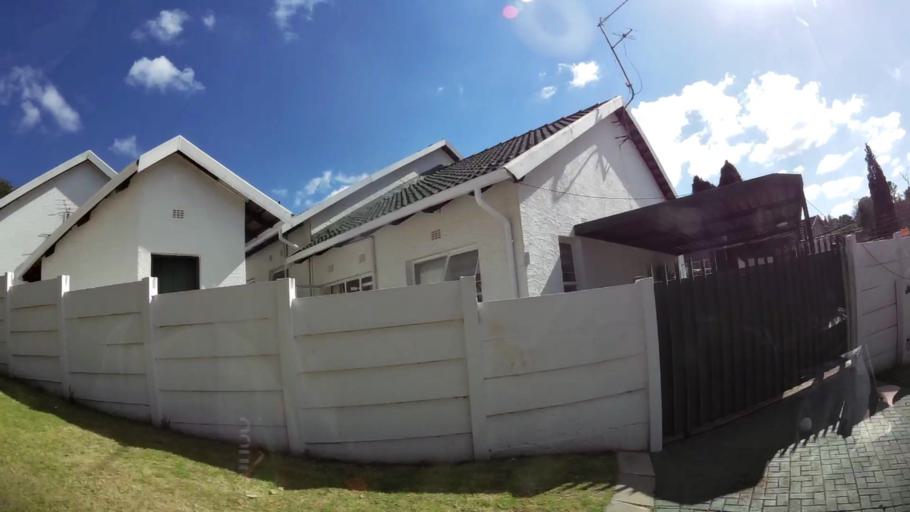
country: ZA
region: Gauteng
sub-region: West Rand District Municipality
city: Krugersdorp
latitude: -26.1195
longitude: 27.8267
